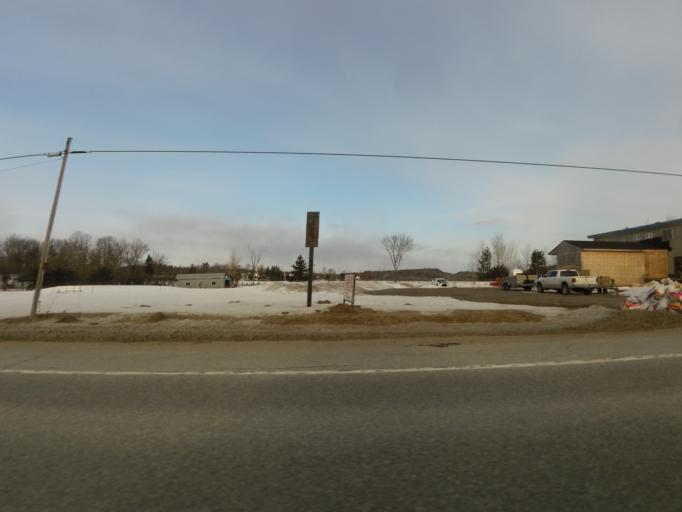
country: CA
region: Quebec
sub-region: Outaouais
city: Wakefield
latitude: 45.8718
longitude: -76.0235
